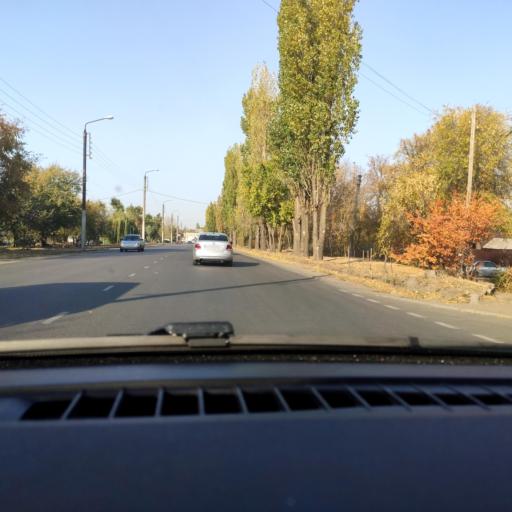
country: RU
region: Voronezj
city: Voronezh
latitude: 51.6215
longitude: 39.1761
